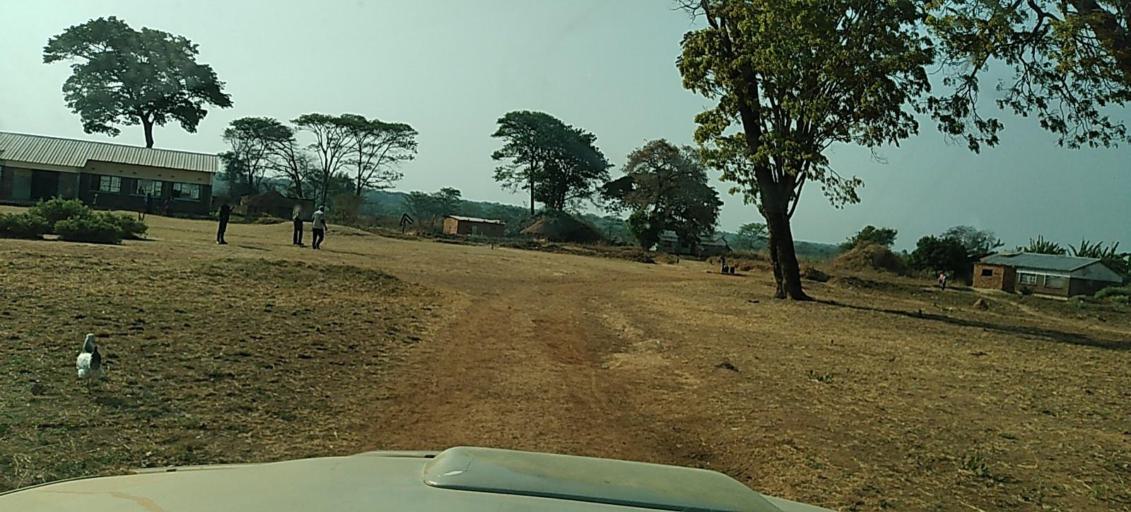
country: ZM
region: North-Western
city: Kasempa
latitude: -13.1859
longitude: 25.9656
